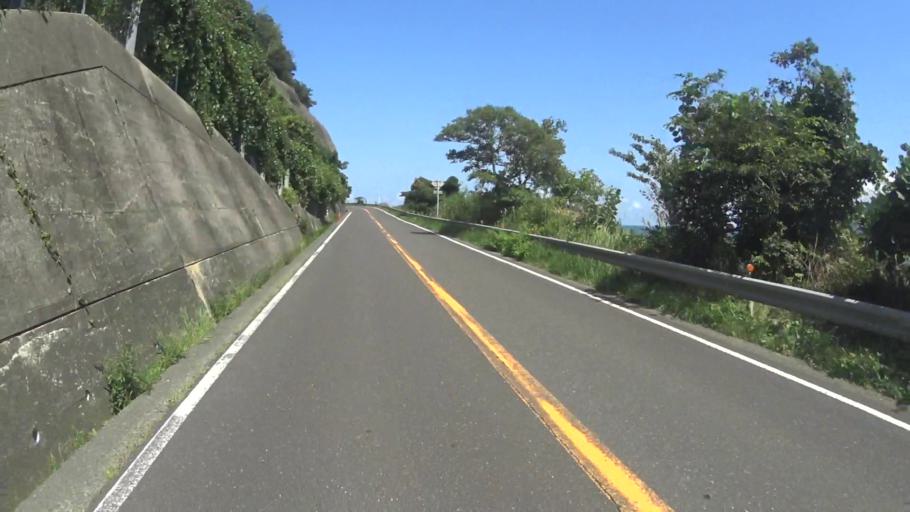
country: JP
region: Kyoto
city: Miyazu
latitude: 35.5259
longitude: 135.2716
